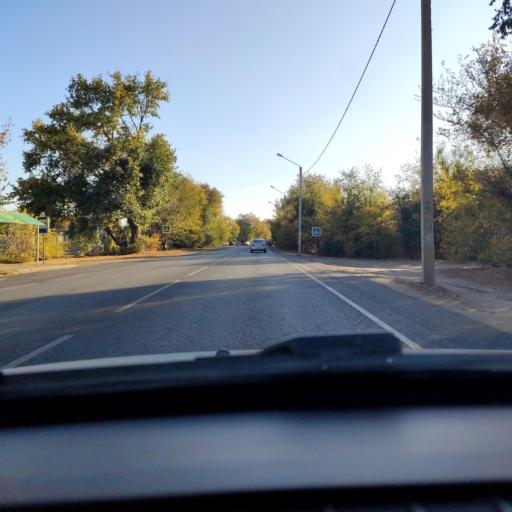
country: RU
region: Voronezj
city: Maslovka
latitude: 51.5898
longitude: 39.1743
